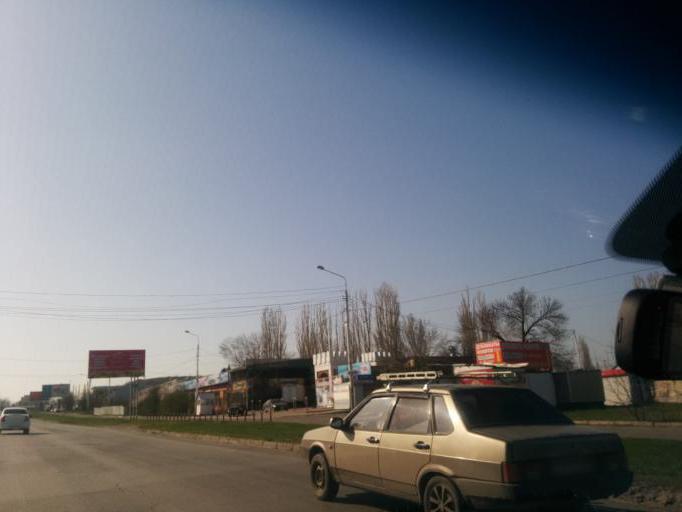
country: RU
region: Rostov
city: Shakhty
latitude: 47.7112
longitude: 40.1622
